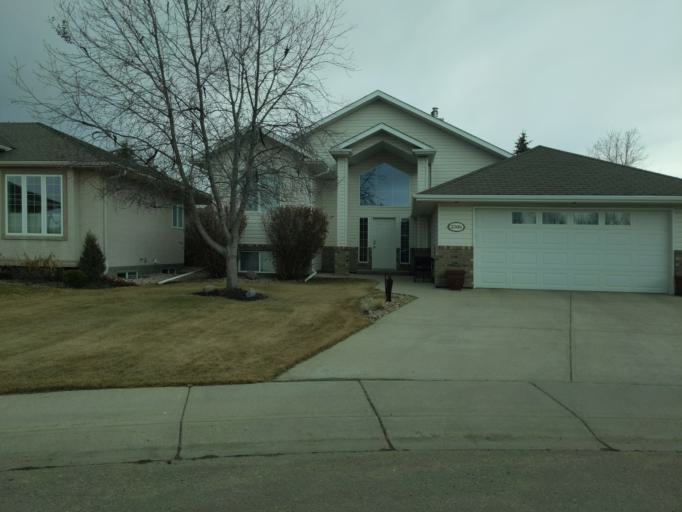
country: CA
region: Saskatchewan
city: Lloydminster
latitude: 53.2575
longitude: -110.0328
